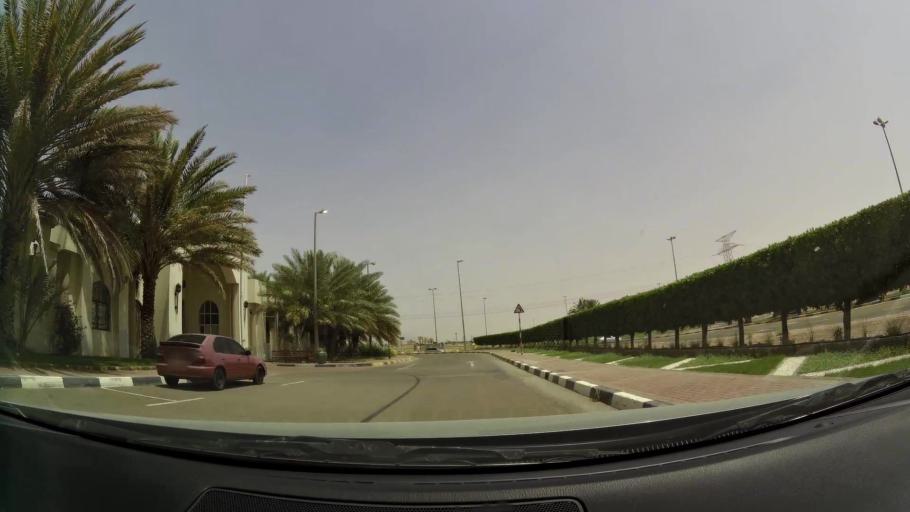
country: AE
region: Abu Dhabi
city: Al Ain
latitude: 24.1856
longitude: 55.6794
